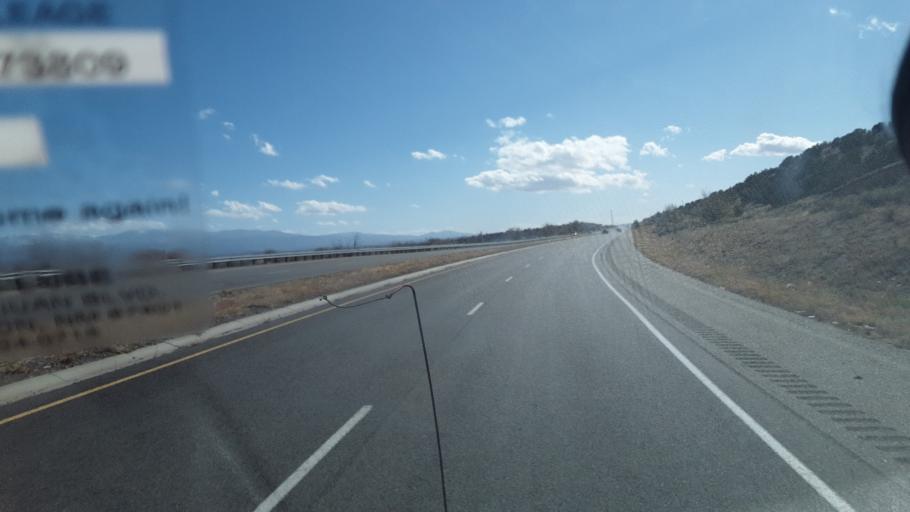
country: US
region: New Mexico
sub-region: Rio Arriba County
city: Ohkay Owingeh
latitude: 36.0353
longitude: -106.0949
